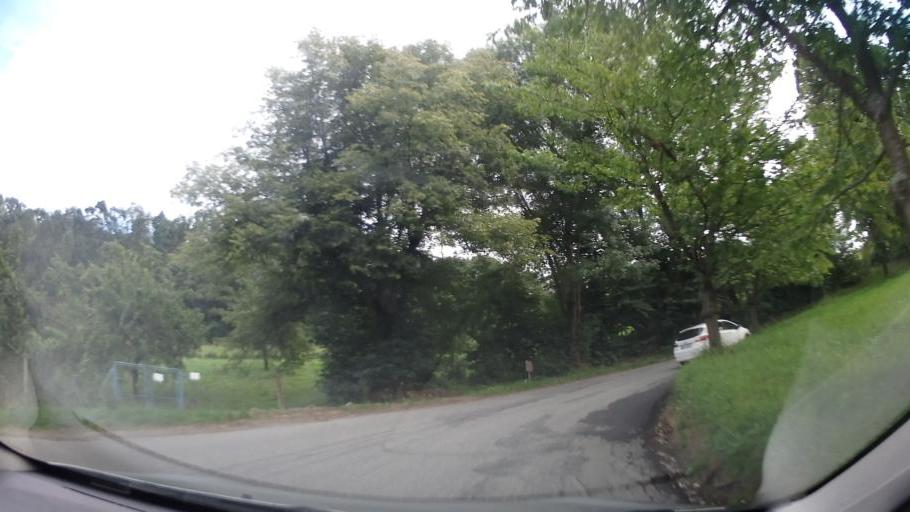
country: CZ
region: Olomoucky
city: Horni Stepanov
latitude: 49.5396
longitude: 16.7201
